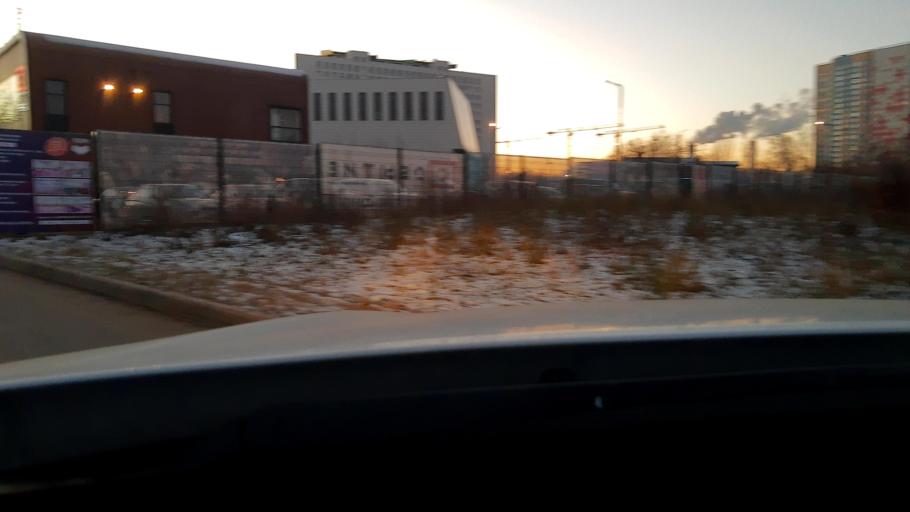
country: RU
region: Moscow
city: Nikol'skoye
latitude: 55.6917
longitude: 37.4778
